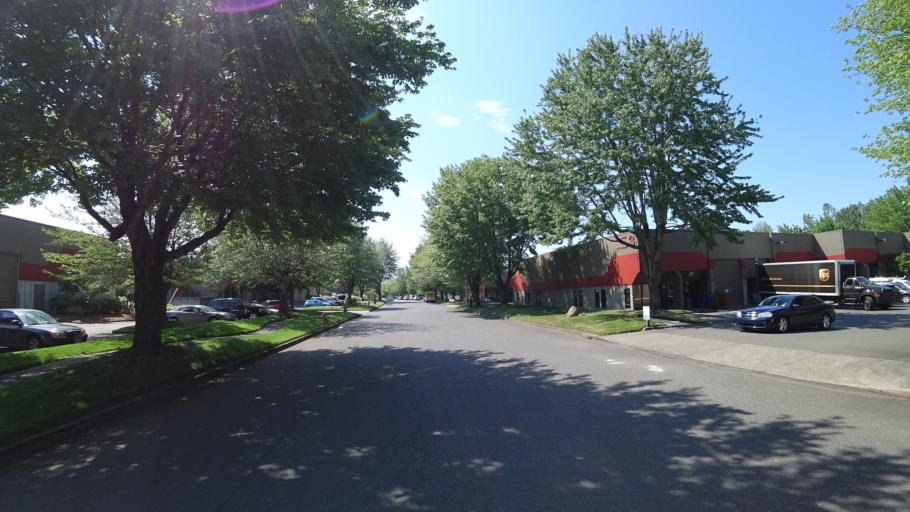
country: US
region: Oregon
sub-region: Multnomah County
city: Lents
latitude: 45.5610
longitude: -122.5406
